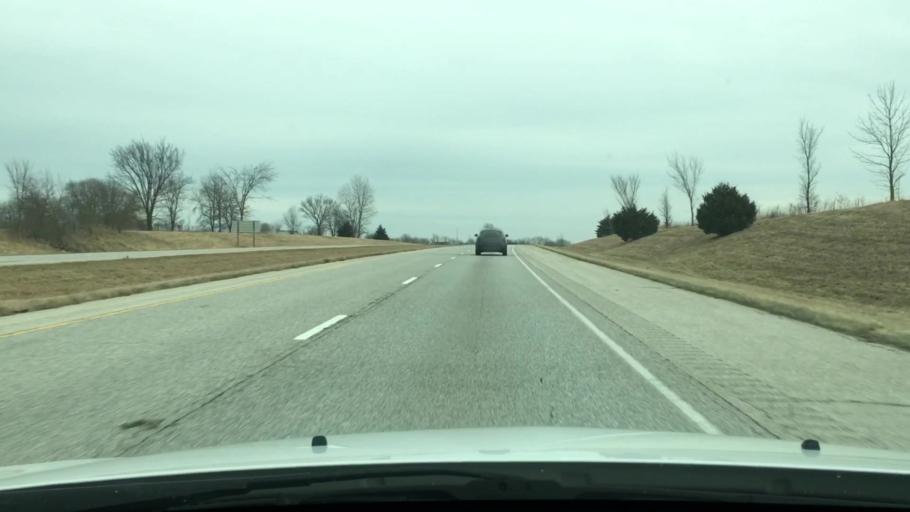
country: US
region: Illinois
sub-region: Pike County
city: Griggsville
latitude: 39.6770
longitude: -90.7306
